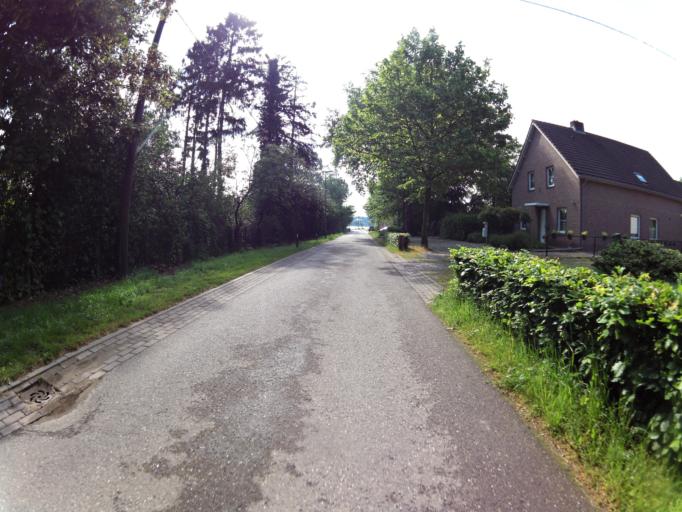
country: DE
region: North Rhine-Westphalia
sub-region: Regierungsbezirk Koln
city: Waldfeucht
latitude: 51.0799
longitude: 5.9905
